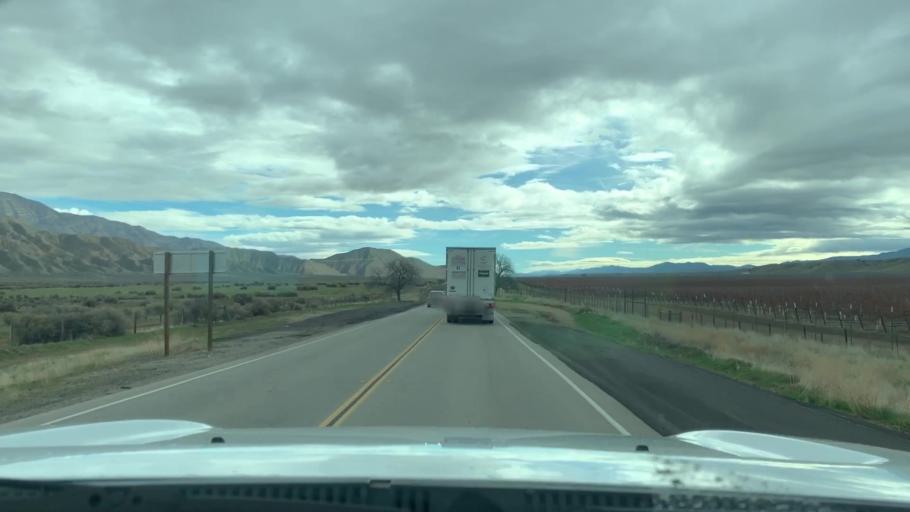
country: US
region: California
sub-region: Kern County
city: Taft Heights
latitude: 35.0342
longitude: -119.8761
